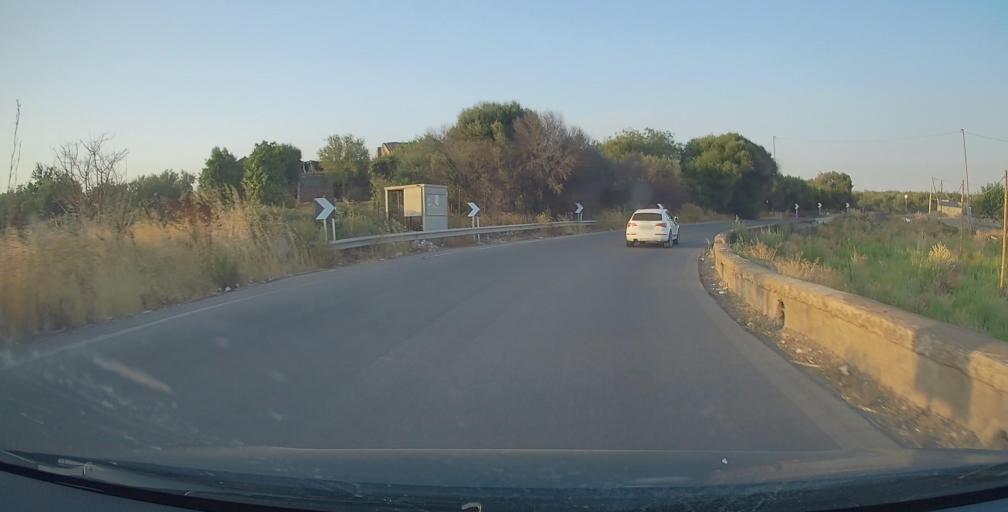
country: IT
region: Sicily
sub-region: Catania
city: Palazzolo
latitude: 37.5484
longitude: 14.9332
